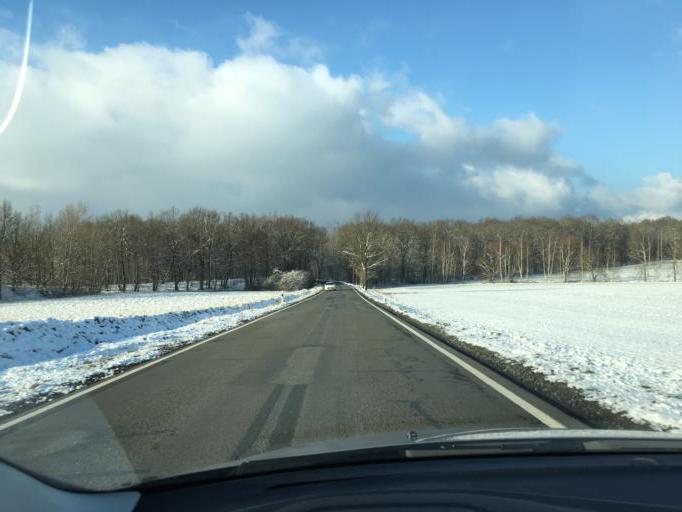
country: DE
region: Saxony
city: Grimma
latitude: 51.2660
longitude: 12.6710
